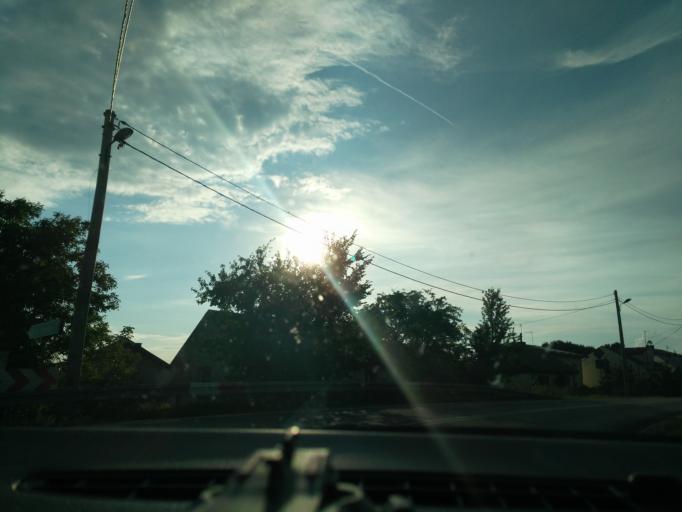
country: PL
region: Lublin Voivodeship
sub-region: Powiat krasnicki
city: Szastarka
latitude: 50.8254
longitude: 22.3116
